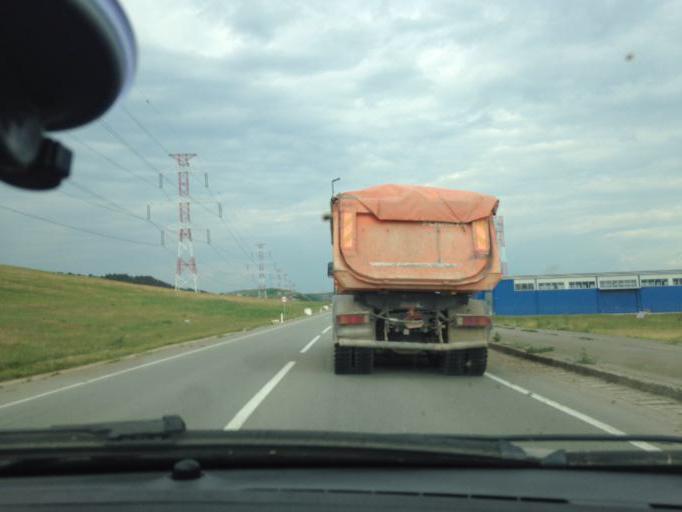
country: RO
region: Cluj
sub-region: Comuna Apahida
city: Sannicoara
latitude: 46.7973
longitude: 23.6616
